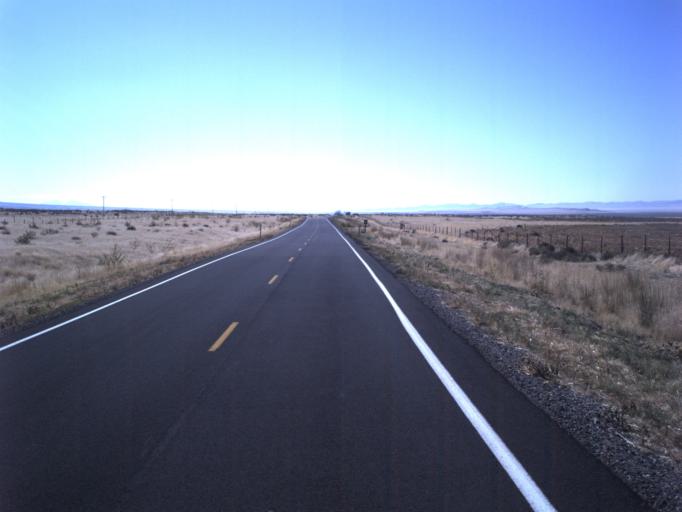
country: US
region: Utah
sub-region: Tooele County
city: Grantsville
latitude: 40.5188
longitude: -112.7477
